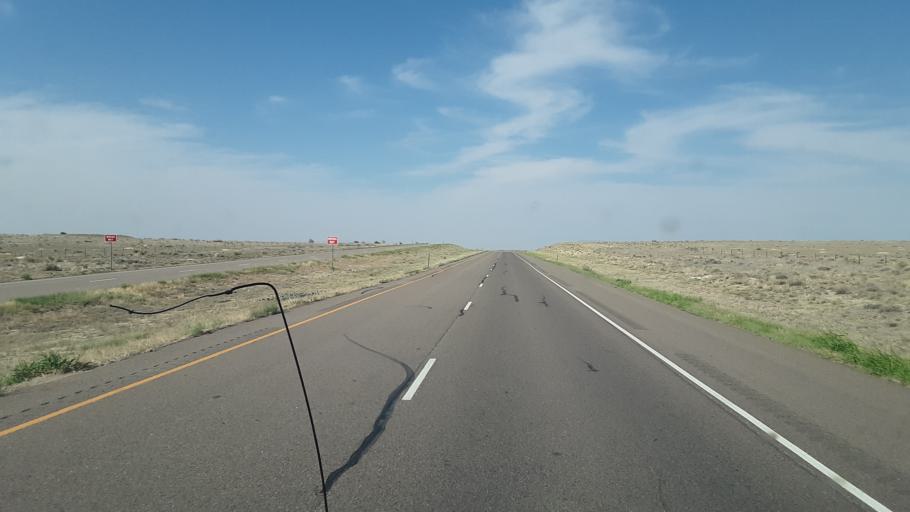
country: US
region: Colorado
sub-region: Otero County
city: La Junta
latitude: 38.0032
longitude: -103.4668
